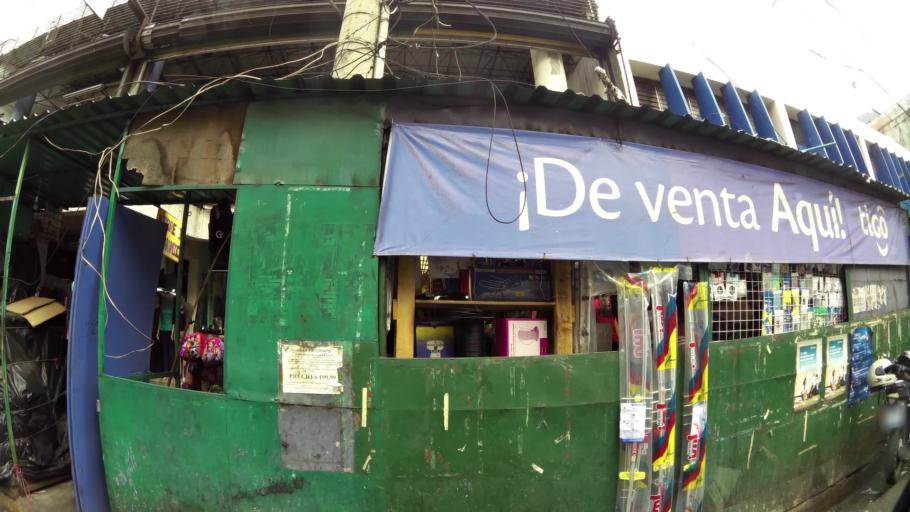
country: SV
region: San Salvador
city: San Salvador
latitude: 13.6985
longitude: -89.1948
